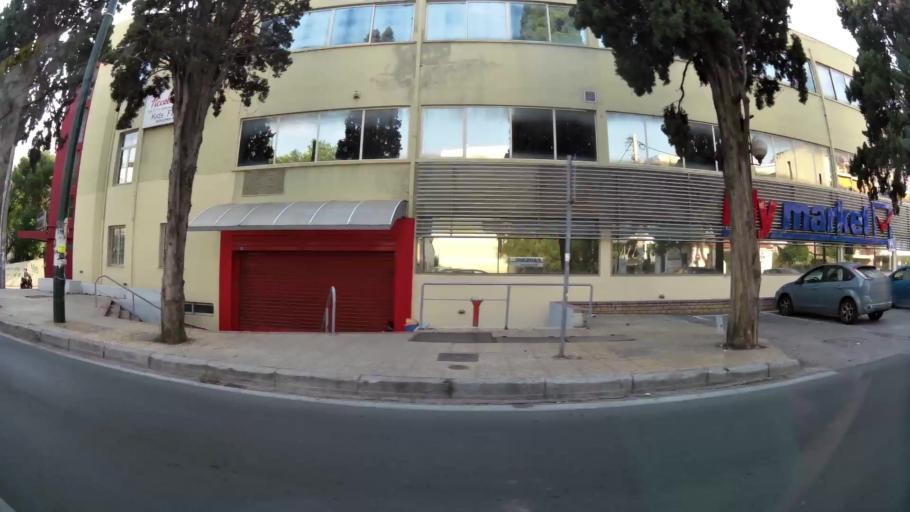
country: GR
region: Attica
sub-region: Nomarchia Athinas
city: Nea Filadelfeia
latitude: 38.0430
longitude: 23.7373
